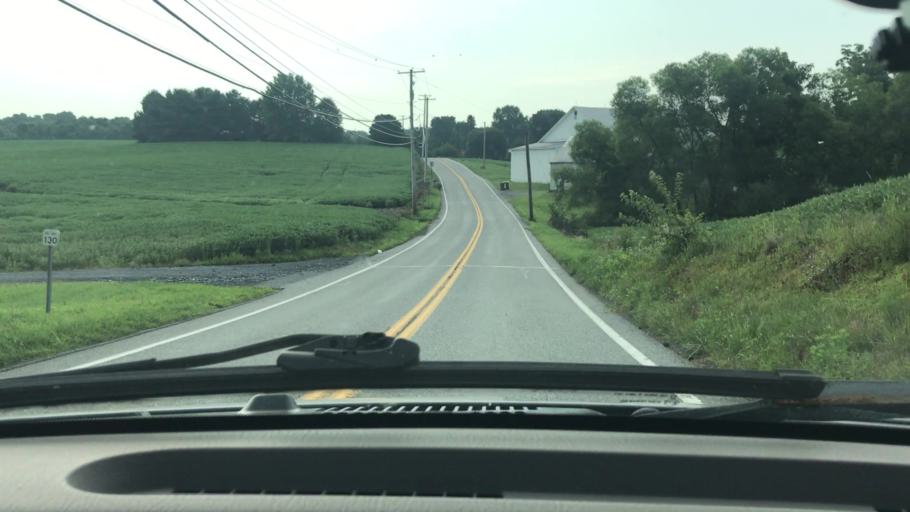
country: US
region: Pennsylvania
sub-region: Dauphin County
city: Middletown
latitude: 40.2213
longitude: -76.7482
